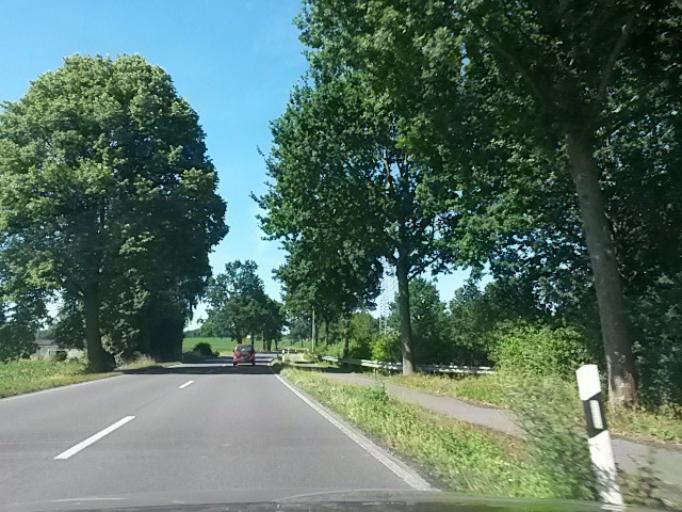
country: DE
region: North Rhine-Westphalia
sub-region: Regierungsbezirk Dusseldorf
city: Grefrath
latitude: 51.3243
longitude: 6.3305
